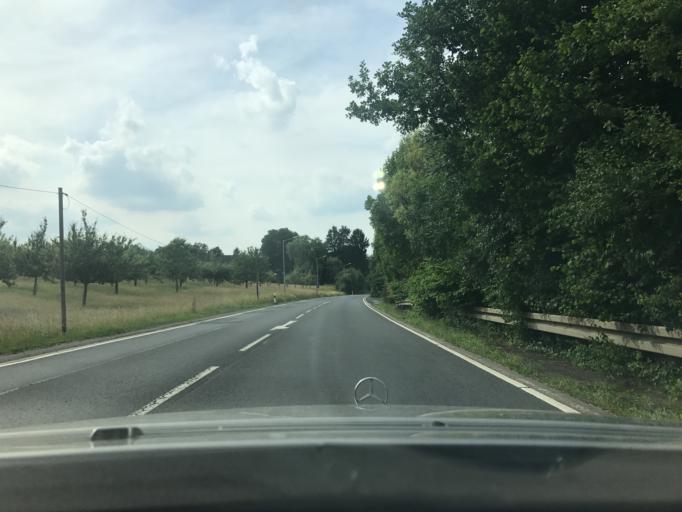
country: DE
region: North Rhine-Westphalia
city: Iserlohn
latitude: 51.4230
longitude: 7.6794
